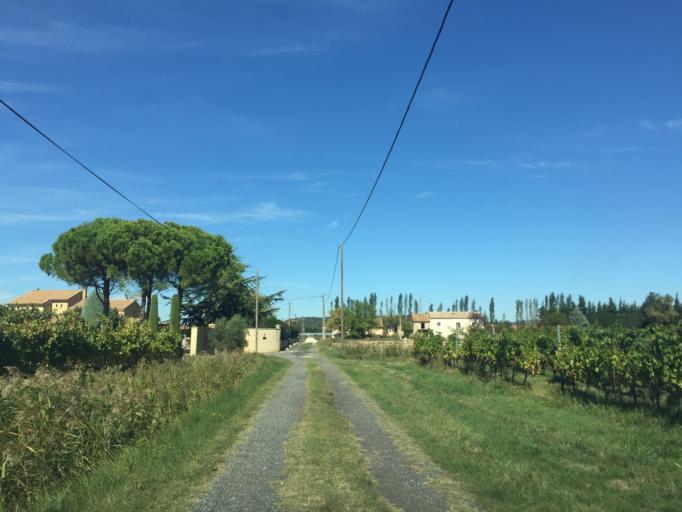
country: FR
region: Provence-Alpes-Cote d'Azur
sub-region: Departement du Vaucluse
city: Piolenc
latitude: 44.1488
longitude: 4.7624
